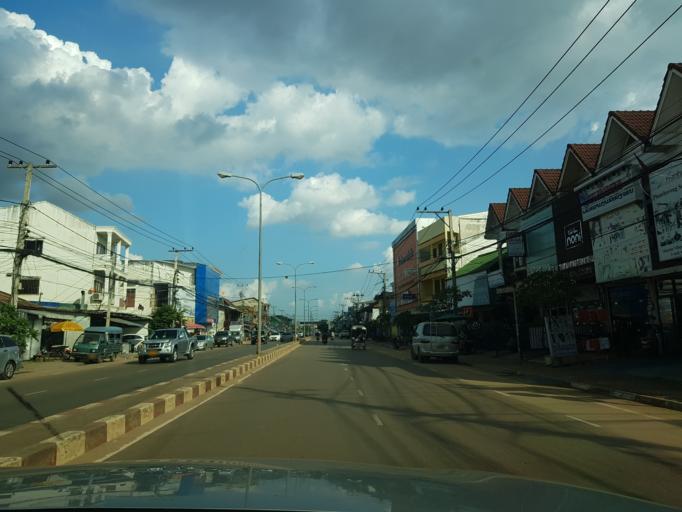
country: TH
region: Nong Khai
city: Si Chiang Mai
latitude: 17.9728
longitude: 102.5638
